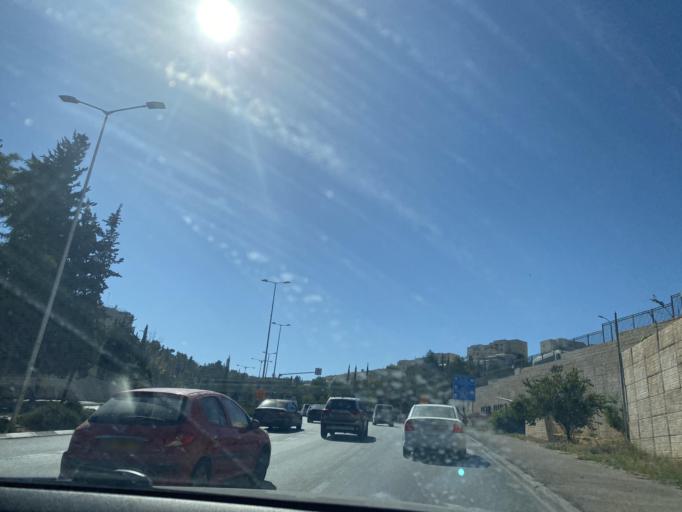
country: PS
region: West Bank
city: Bayt Iksa
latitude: 31.8121
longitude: 35.2024
